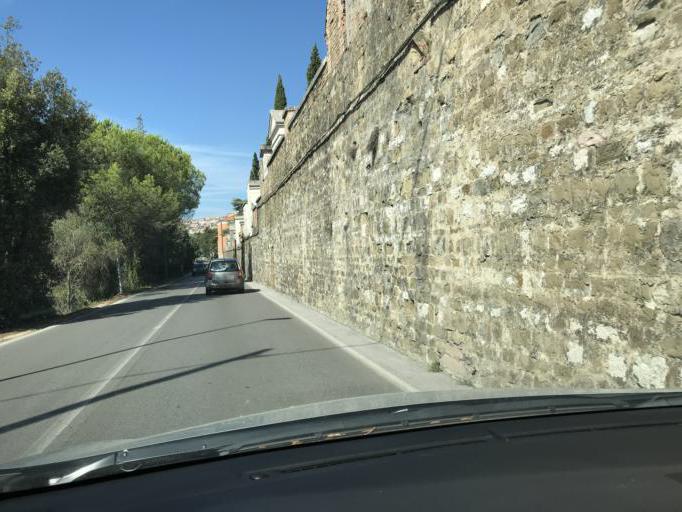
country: IT
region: Umbria
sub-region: Provincia di Perugia
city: Perugia
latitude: 43.1104
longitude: 12.4140
